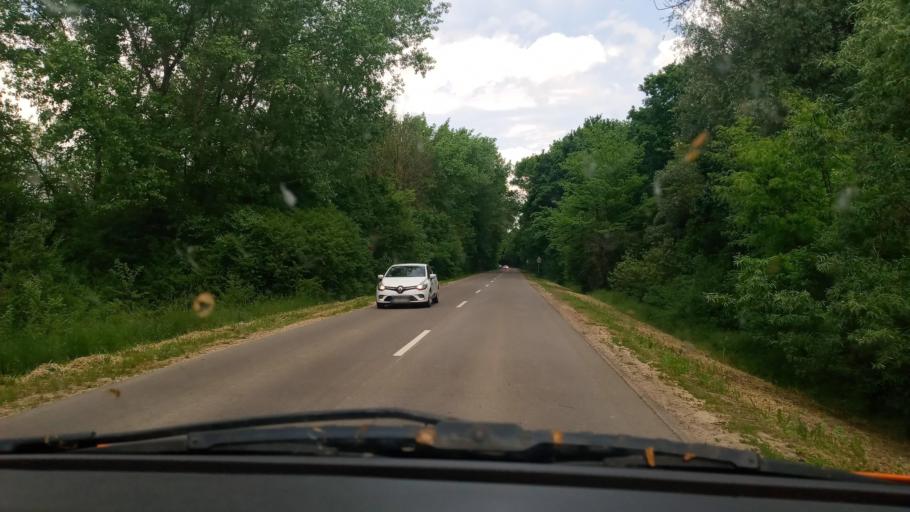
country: HU
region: Baranya
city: Villany
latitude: 45.8526
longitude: 18.4804
